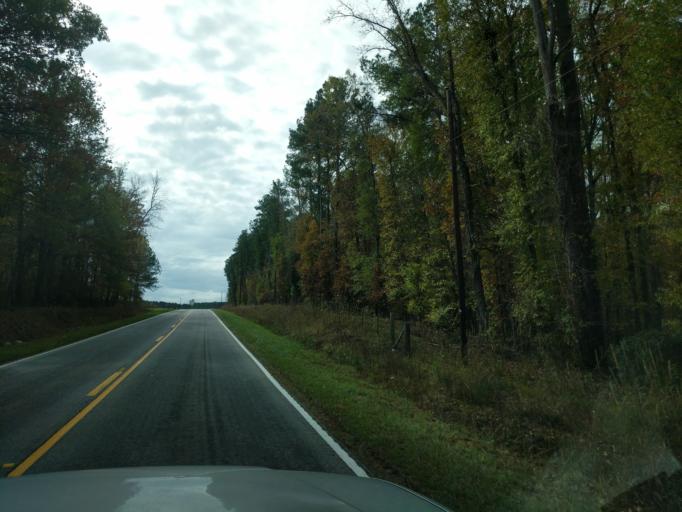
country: US
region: South Carolina
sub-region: Greenwood County
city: Ninety Six
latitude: 34.2075
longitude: -81.8844
